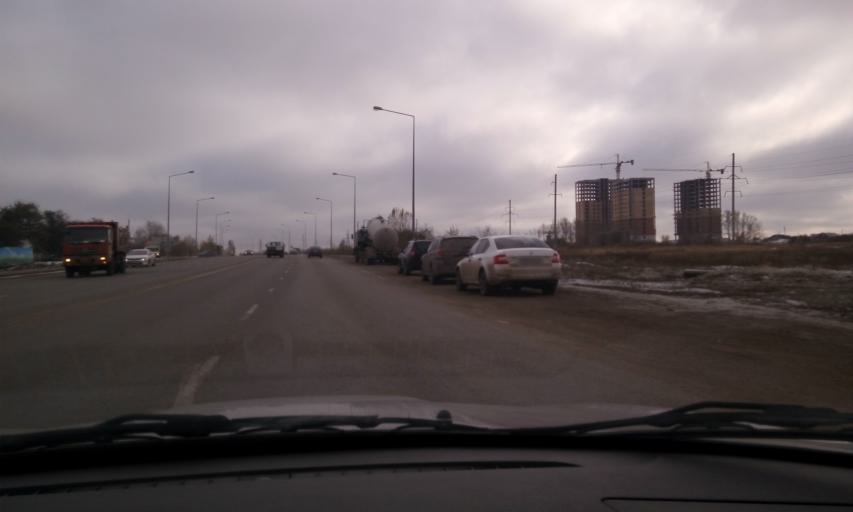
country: KZ
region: Astana Qalasy
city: Astana
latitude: 51.1365
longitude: 71.5346
